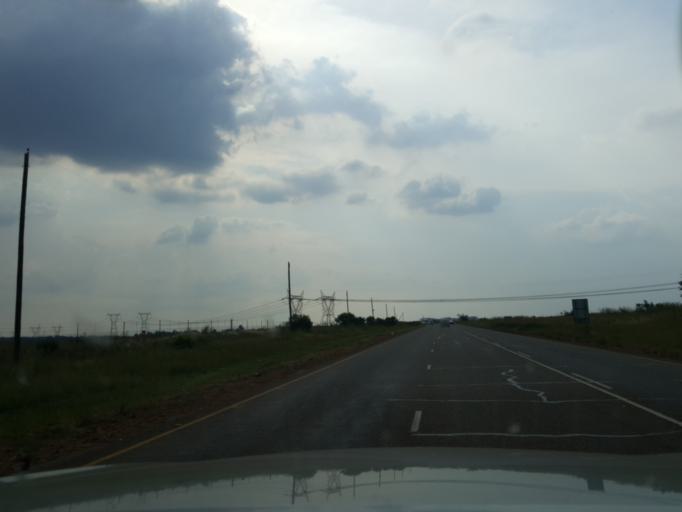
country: ZA
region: Gauteng
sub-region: City of Tshwane Metropolitan Municipality
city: Centurion
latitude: -25.8530
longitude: 28.2934
